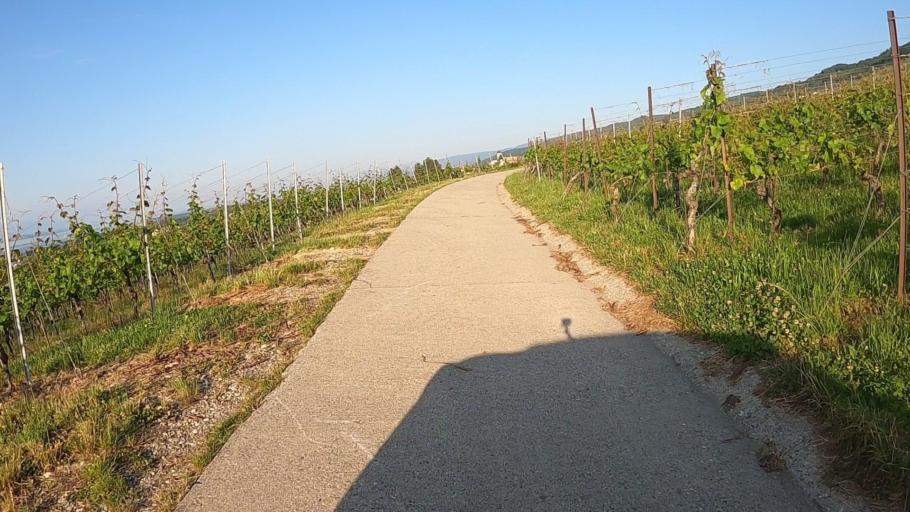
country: CH
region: Vaud
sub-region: Nyon District
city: Rolle
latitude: 46.4729
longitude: 6.3439
